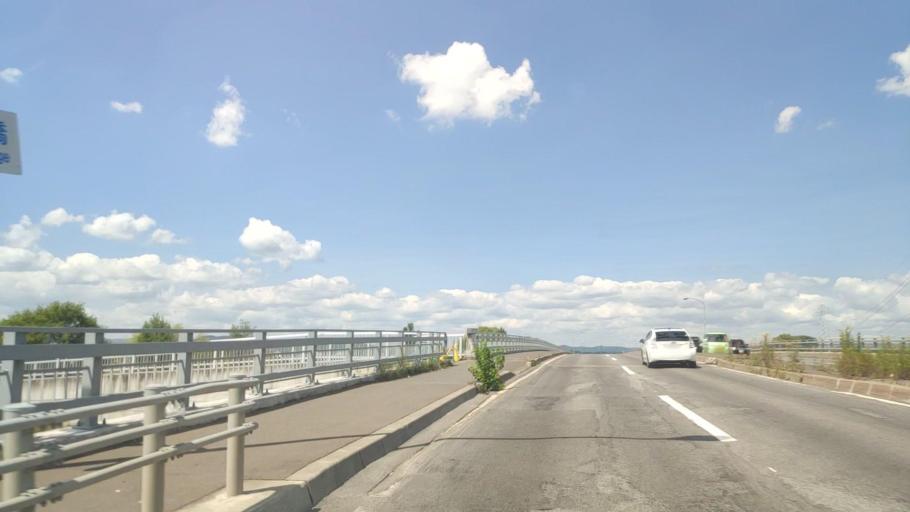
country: JP
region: Hokkaido
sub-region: Asahikawa-shi
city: Asahikawa
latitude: 43.7964
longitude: 142.3977
